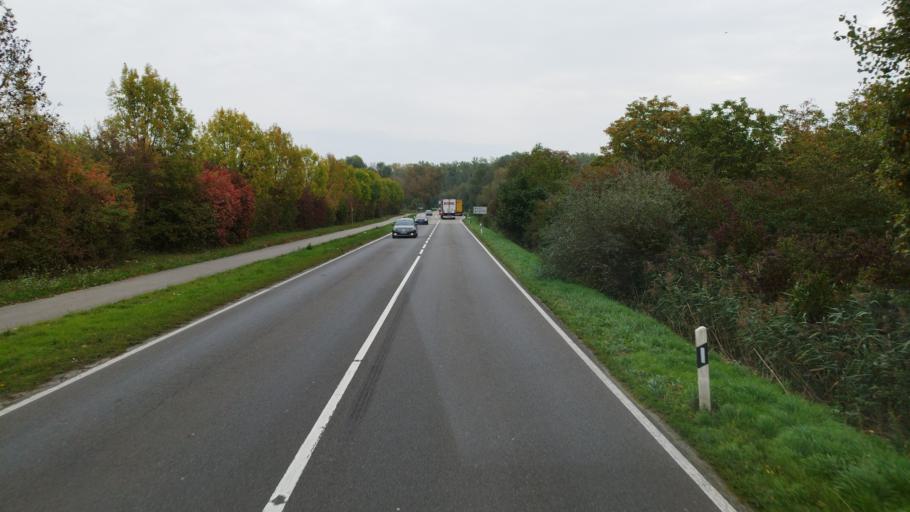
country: DE
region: Rheinland-Pfalz
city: Worth am Rhein
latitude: 49.0640
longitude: 8.2907
